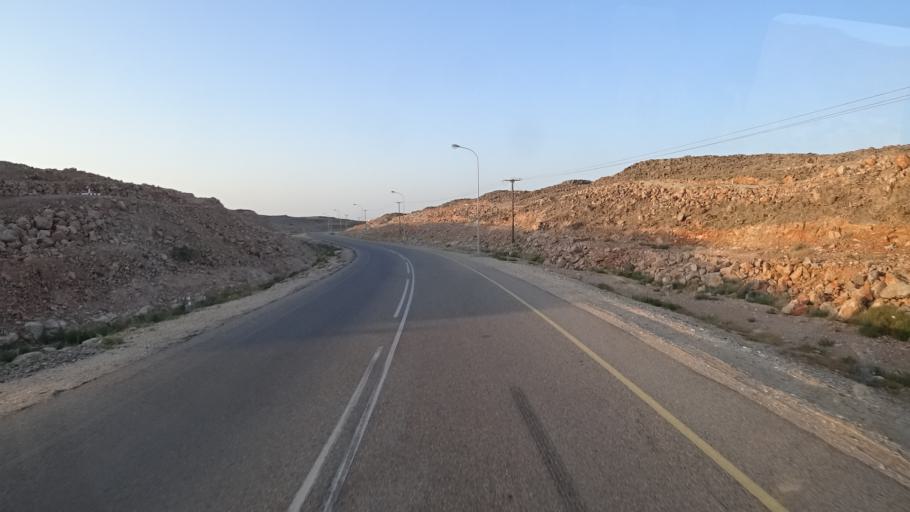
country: OM
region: Ash Sharqiyah
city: Sur
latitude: 22.5032
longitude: 59.7923
